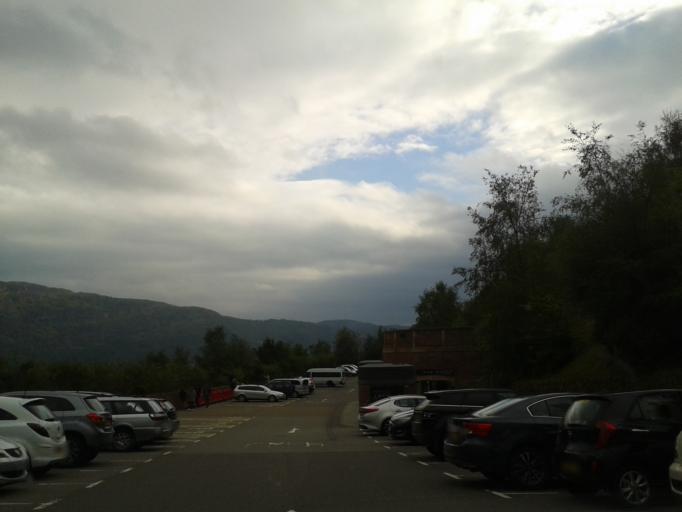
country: GB
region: Scotland
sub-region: Highland
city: Beauly
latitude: 57.3244
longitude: -4.4446
